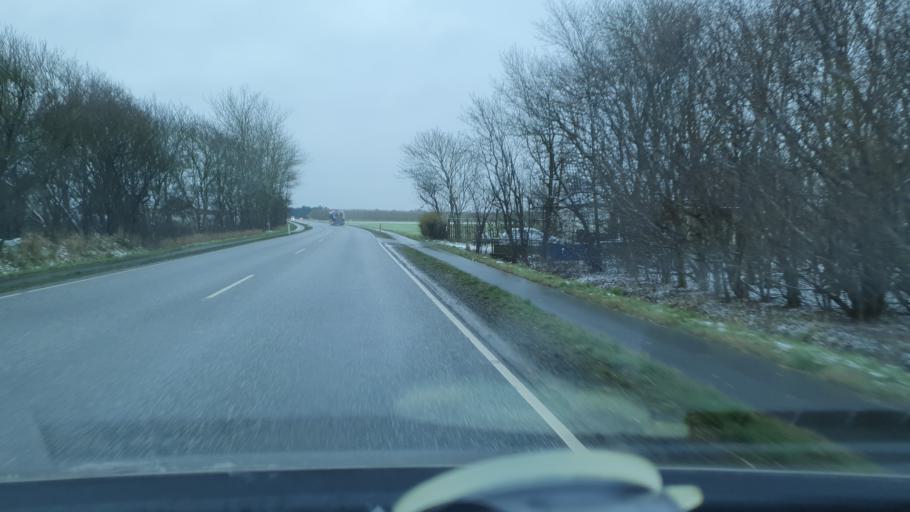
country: DK
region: North Denmark
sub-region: Jammerbugt Kommune
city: Brovst
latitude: 57.1163
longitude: 9.6063
